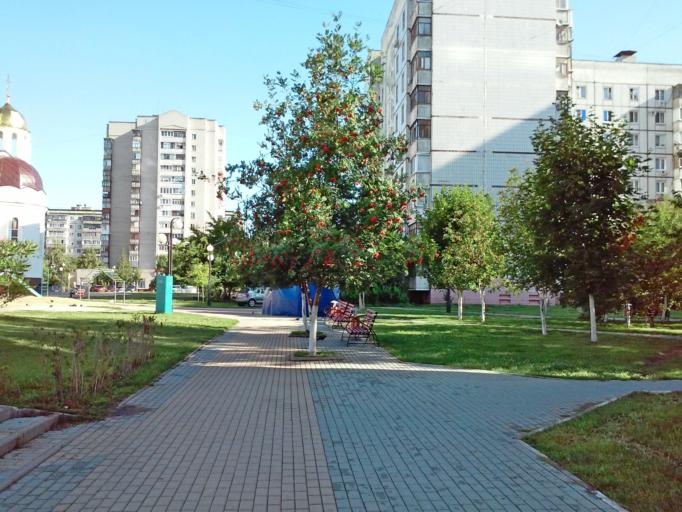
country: RU
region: Belgorod
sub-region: Belgorodskiy Rayon
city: Belgorod
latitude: 50.5604
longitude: 36.5672
